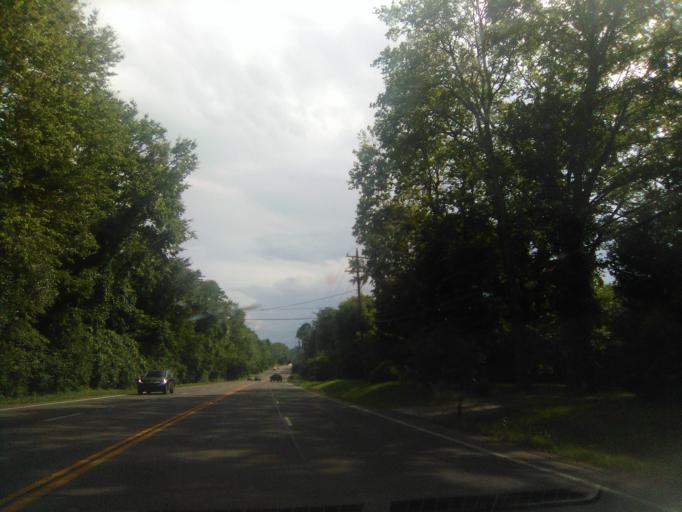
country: US
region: Tennessee
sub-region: Davidson County
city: Belle Meade
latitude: 36.0948
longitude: -86.8751
